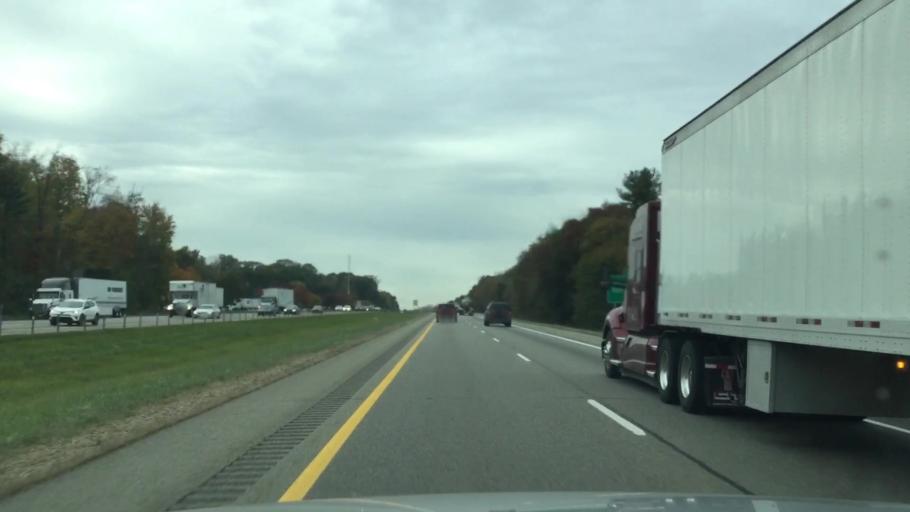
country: US
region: Michigan
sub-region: Calhoun County
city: Lakeview
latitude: 42.2639
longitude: -85.2143
